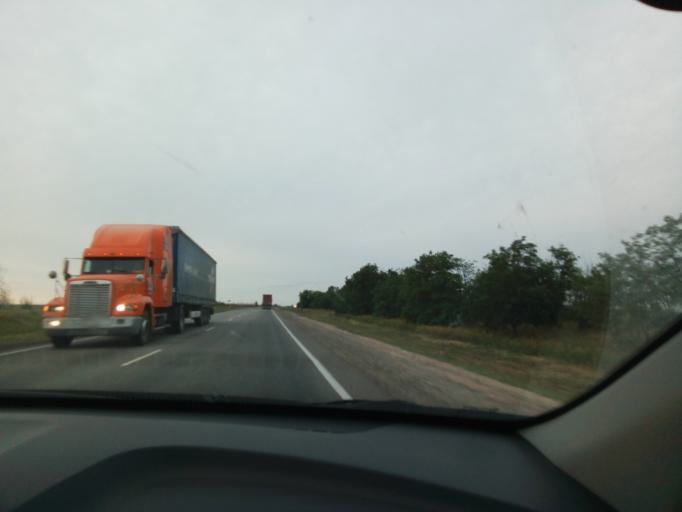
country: RU
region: Volgograd
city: Dubovka
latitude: 49.1436
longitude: 44.8293
